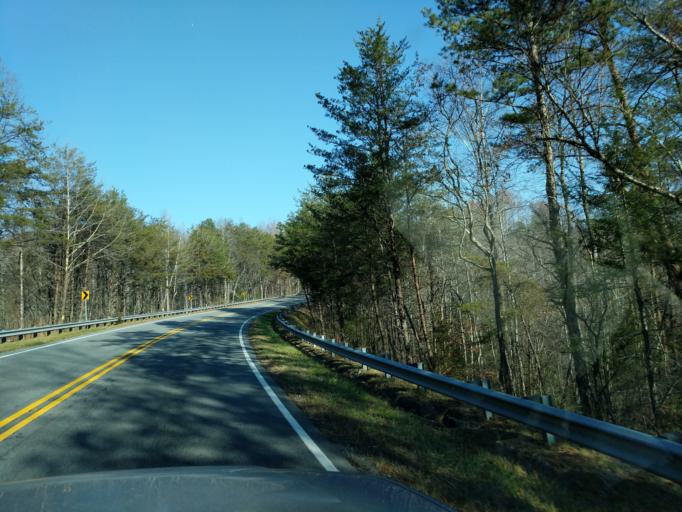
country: US
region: North Carolina
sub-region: McDowell County
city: West Marion
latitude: 35.5537
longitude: -81.9688
